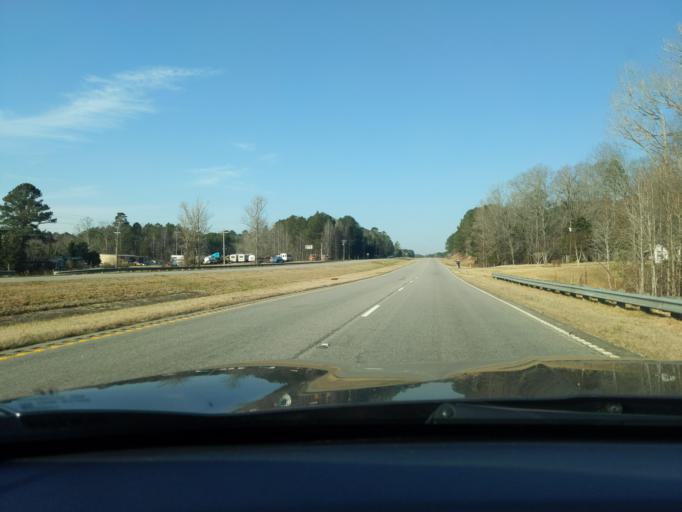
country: US
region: South Carolina
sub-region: Greenwood County
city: Greenwood
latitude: 34.1898
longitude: -82.2576
